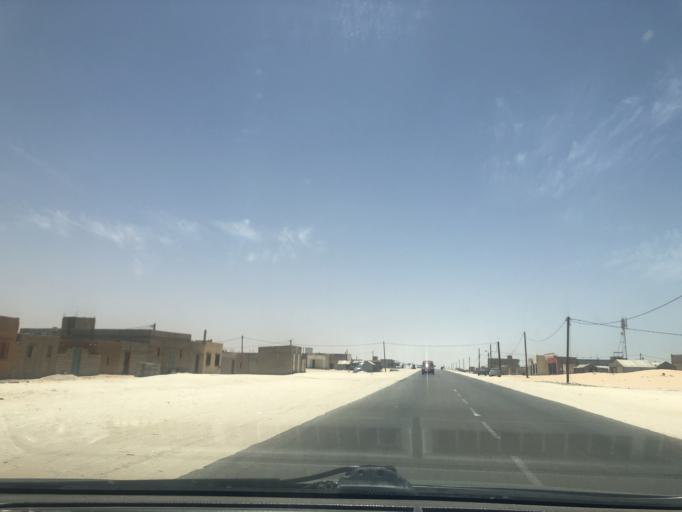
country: MR
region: Nouakchott
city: Nouakchott
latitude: 18.0081
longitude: -15.9596
